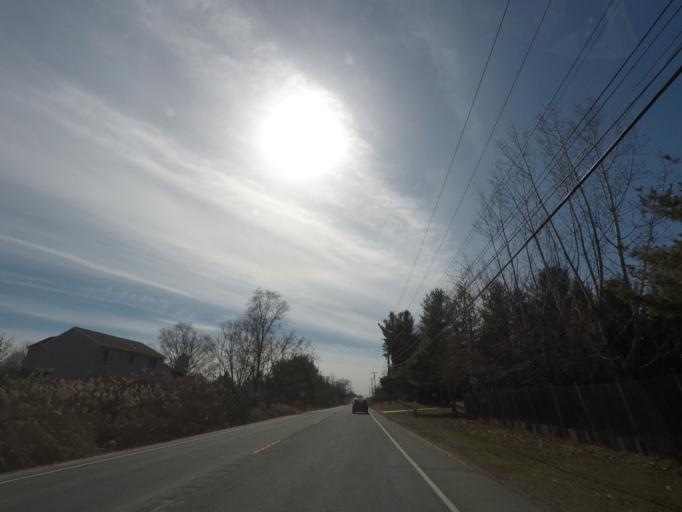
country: US
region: New York
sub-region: Albany County
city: Cohoes
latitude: 42.7651
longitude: -73.7446
